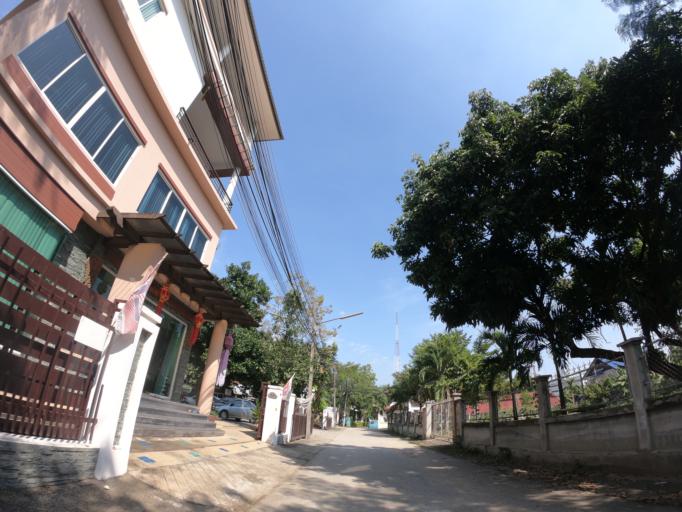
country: TH
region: Chiang Mai
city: Chiang Mai
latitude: 18.7761
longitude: 99.0244
